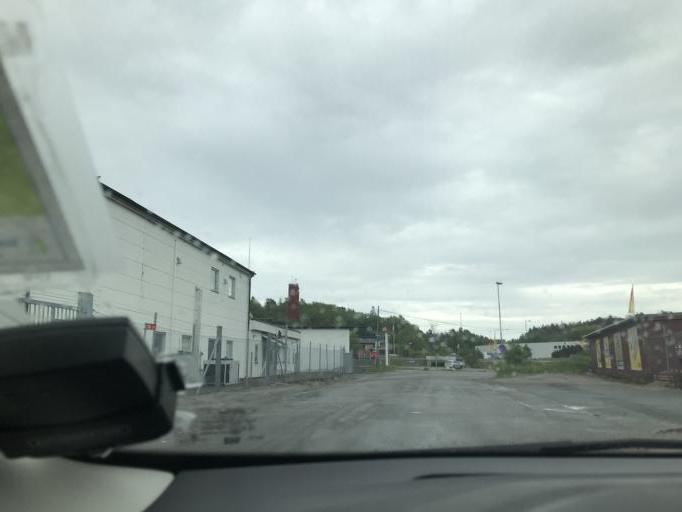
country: SE
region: Stockholm
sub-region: Botkyrka Kommun
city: Tumba
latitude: 59.2154
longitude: 17.8273
